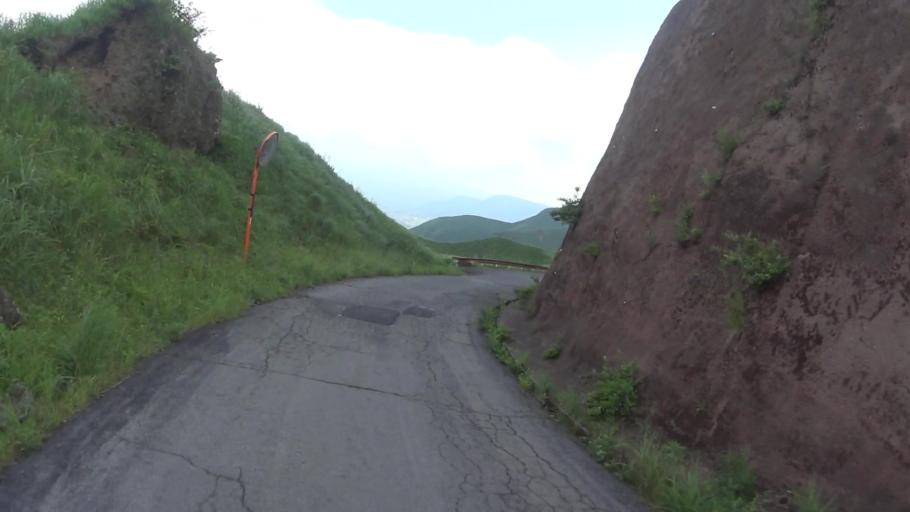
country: JP
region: Kumamoto
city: Aso
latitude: 32.9626
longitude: 131.0029
